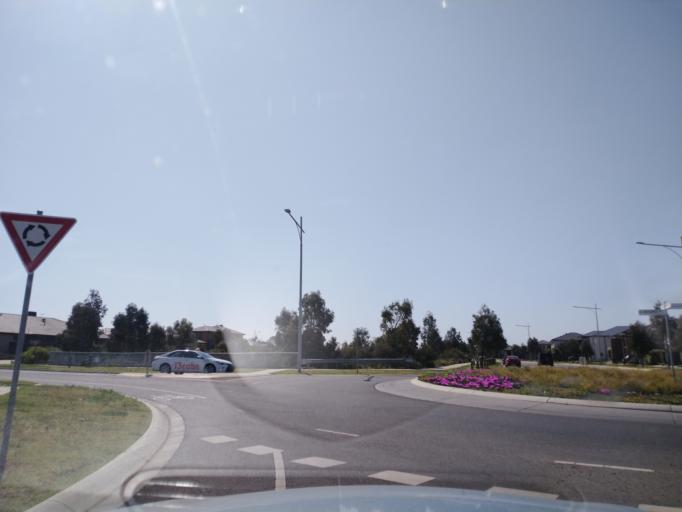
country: AU
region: Victoria
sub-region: Wyndham
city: Williams Landing
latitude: -37.8441
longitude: 144.7403
